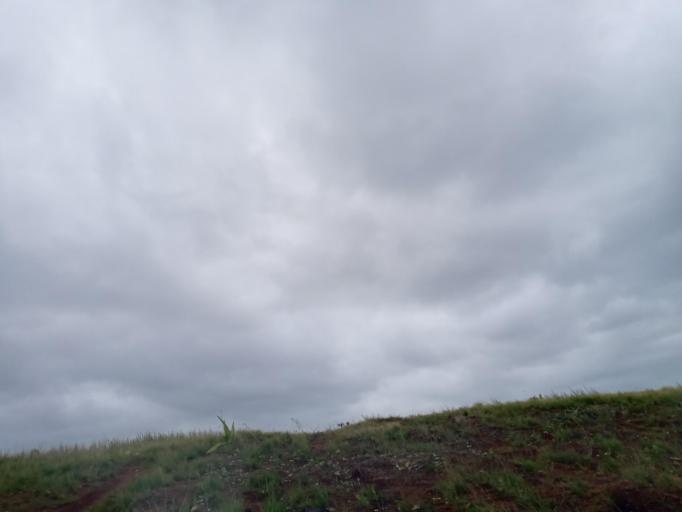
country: MG
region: Atsimo-Atsinanana
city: Vohipaho
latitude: -23.9085
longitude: 47.5178
